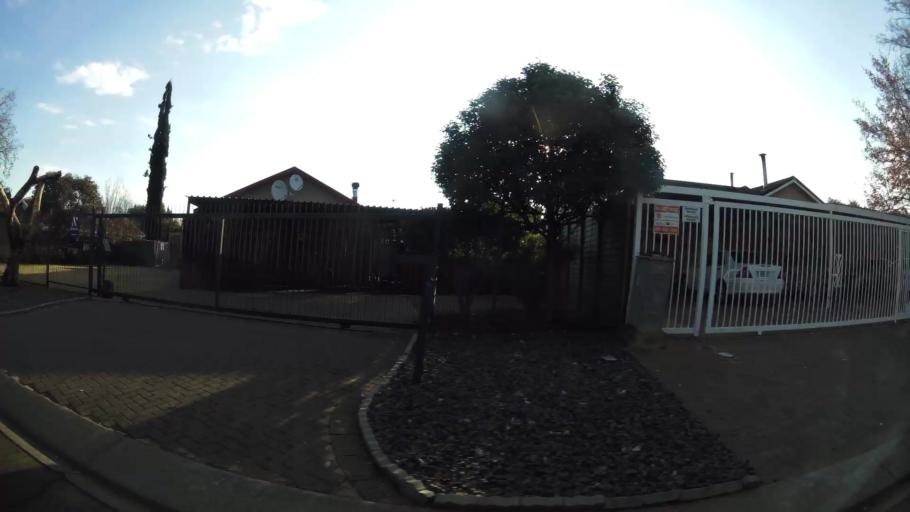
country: ZA
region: Orange Free State
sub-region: Mangaung Metropolitan Municipality
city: Bloemfontein
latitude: -29.1575
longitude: 26.1845
